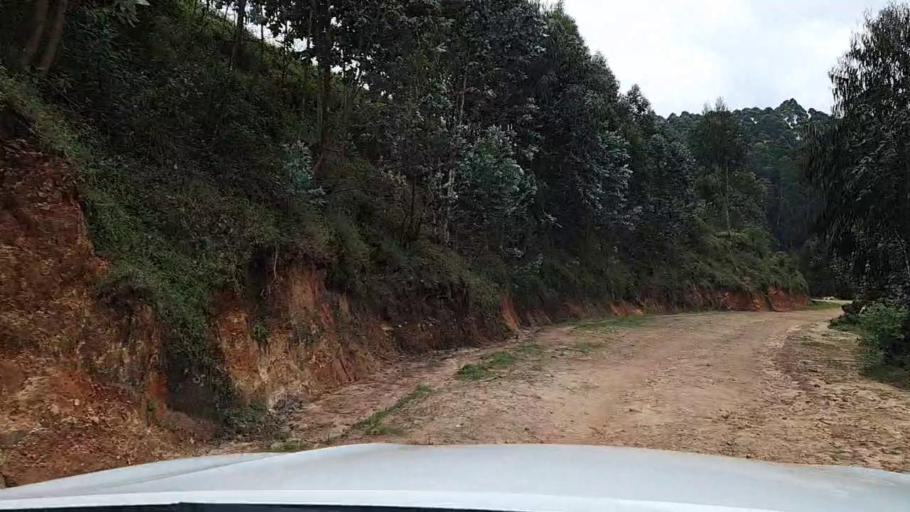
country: RW
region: Western Province
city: Kibuye
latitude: -2.2814
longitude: 29.3680
